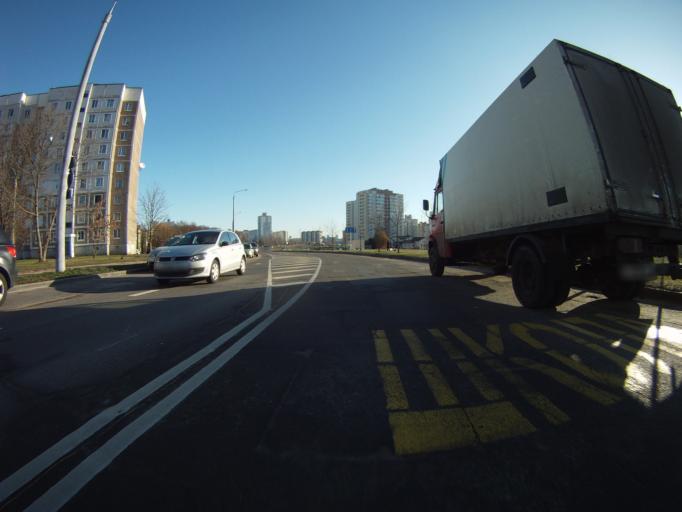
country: BY
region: Minsk
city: Novoye Medvezhino
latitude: 53.8798
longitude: 27.4412
